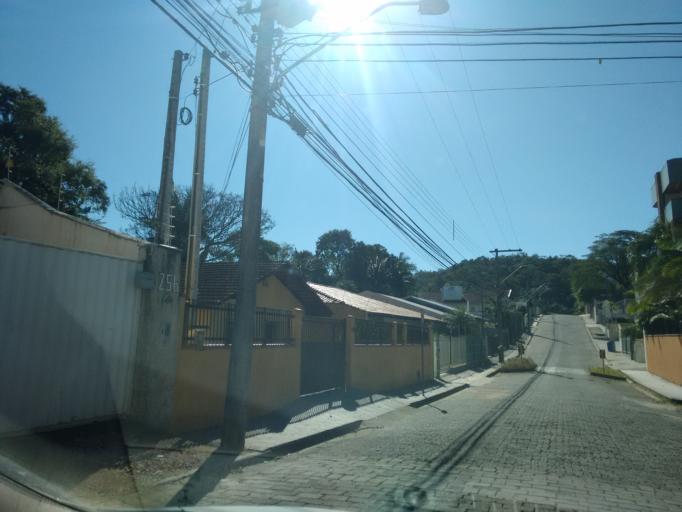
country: BR
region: Santa Catarina
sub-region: Blumenau
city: Blumenau
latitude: -26.8901
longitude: -49.0940
